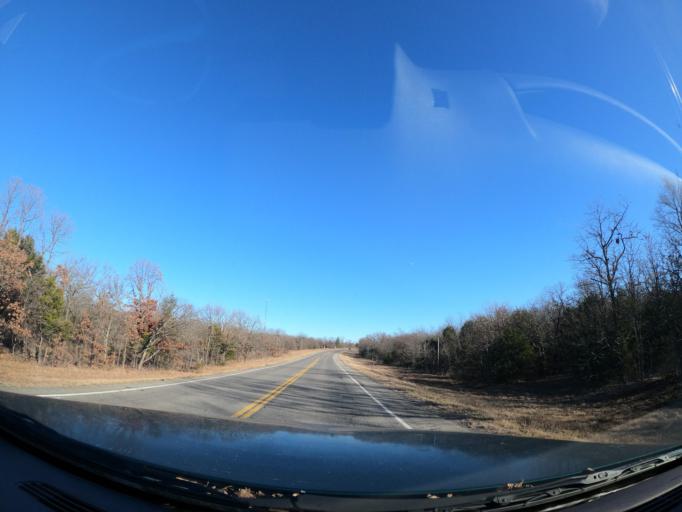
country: US
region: Oklahoma
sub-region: Pittsburg County
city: Longtown
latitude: 35.2251
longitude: -95.4364
